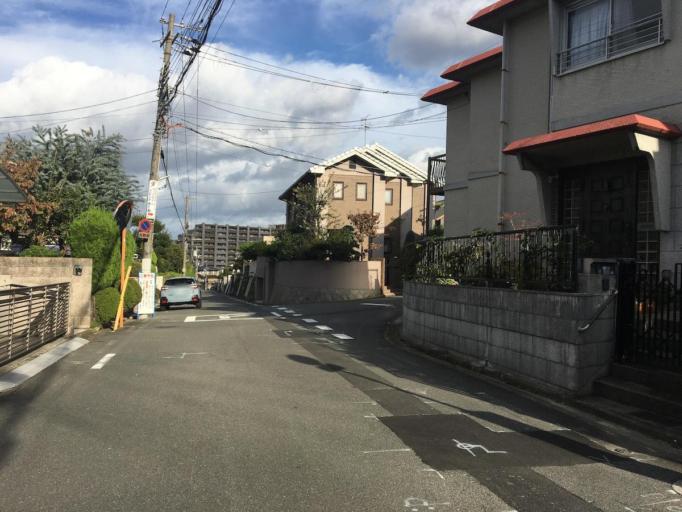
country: JP
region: Osaka
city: Suita
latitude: 34.8001
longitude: 135.5169
